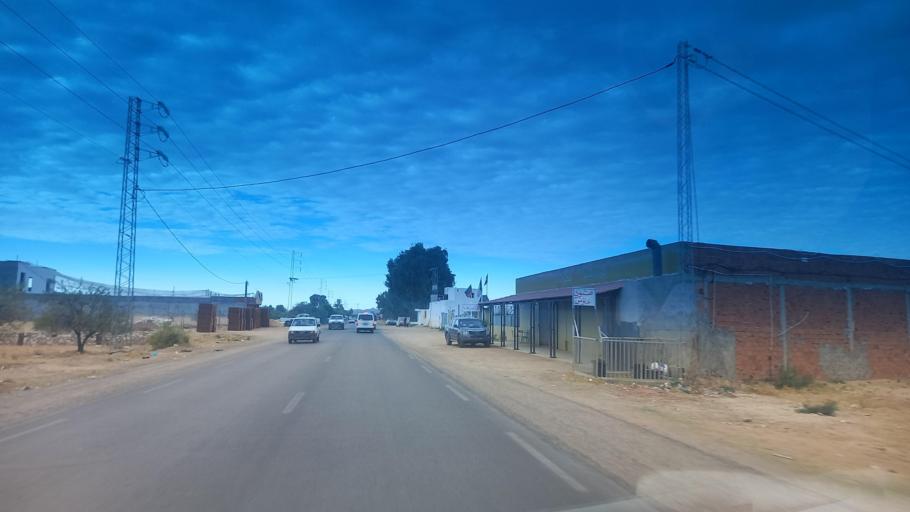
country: TN
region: Al Qasrayn
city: Kasserine
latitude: 35.2637
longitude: 9.0928
